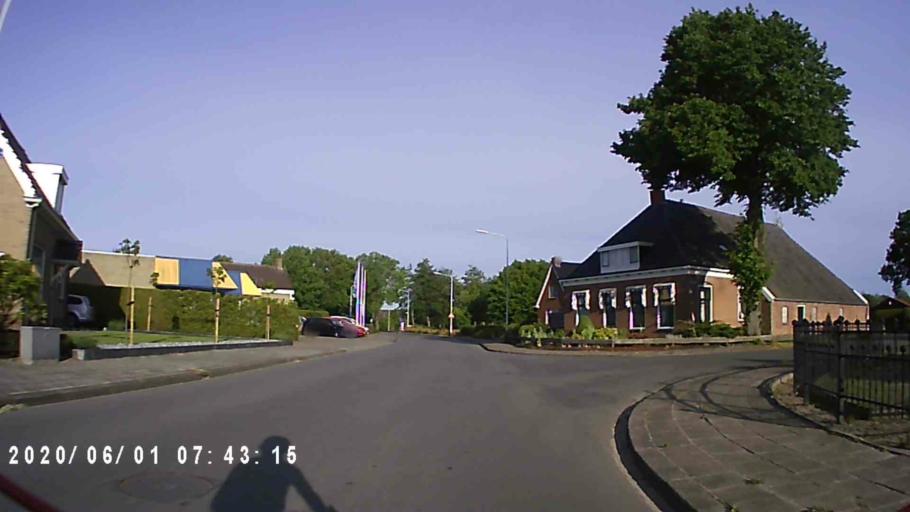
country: NL
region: Friesland
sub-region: Gemeente Dantumadiel
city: Damwald
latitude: 53.2907
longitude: 5.9737
